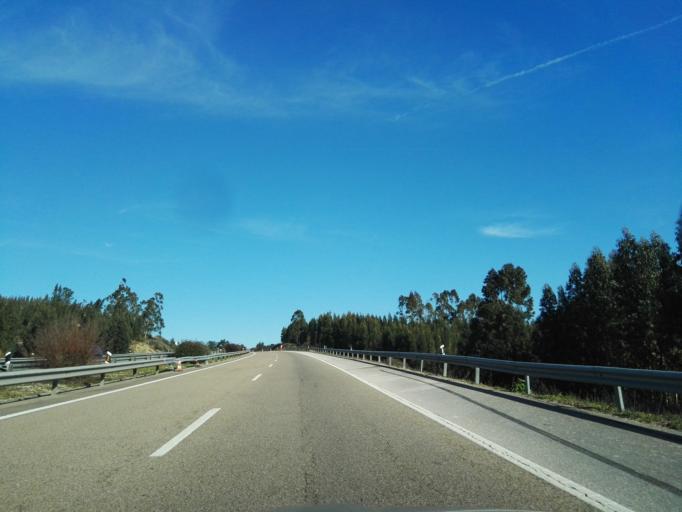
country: PT
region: Santarem
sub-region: Constancia
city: Constancia
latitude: 39.4880
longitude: -8.3163
